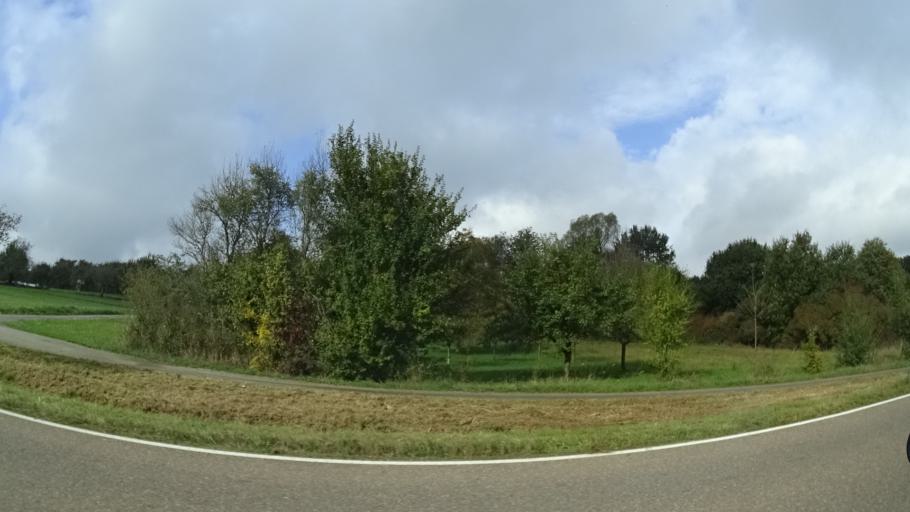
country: DE
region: Baden-Wuerttemberg
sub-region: Karlsruhe Region
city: Ubstadt-Weiher
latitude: 49.1869
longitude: 8.6746
